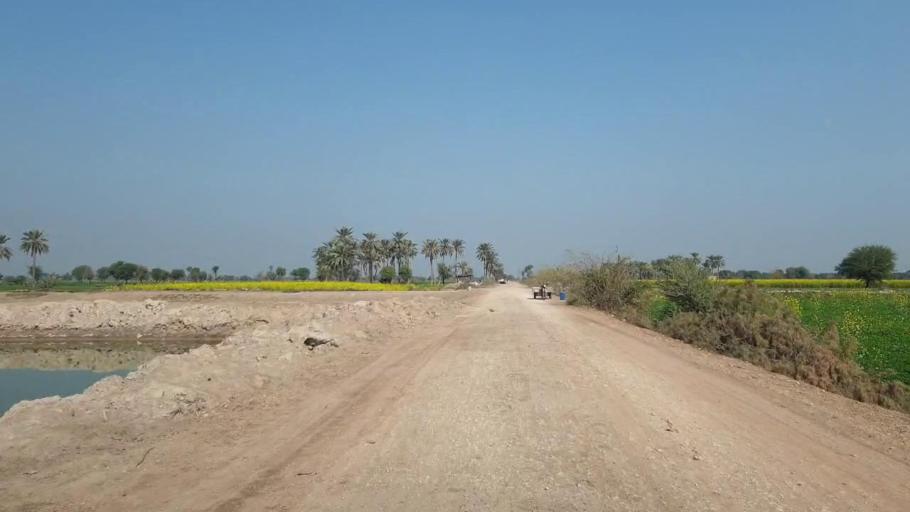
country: PK
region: Sindh
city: Hala
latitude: 25.9059
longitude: 68.4197
